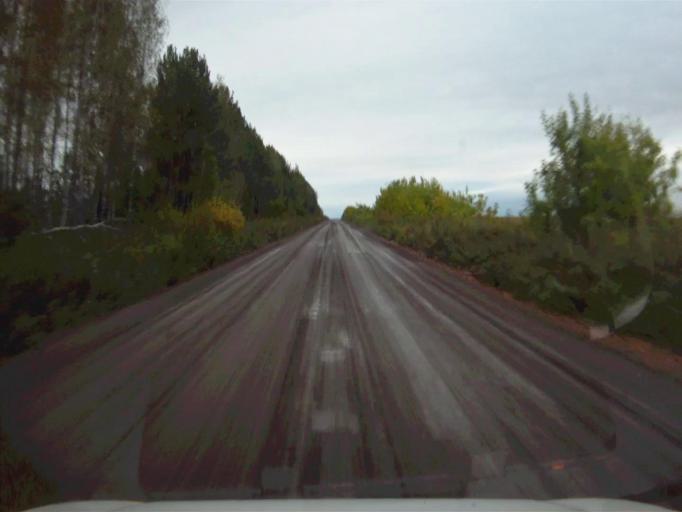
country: RU
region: Sverdlovsk
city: Mikhaylovsk
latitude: 56.1531
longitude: 59.2645
